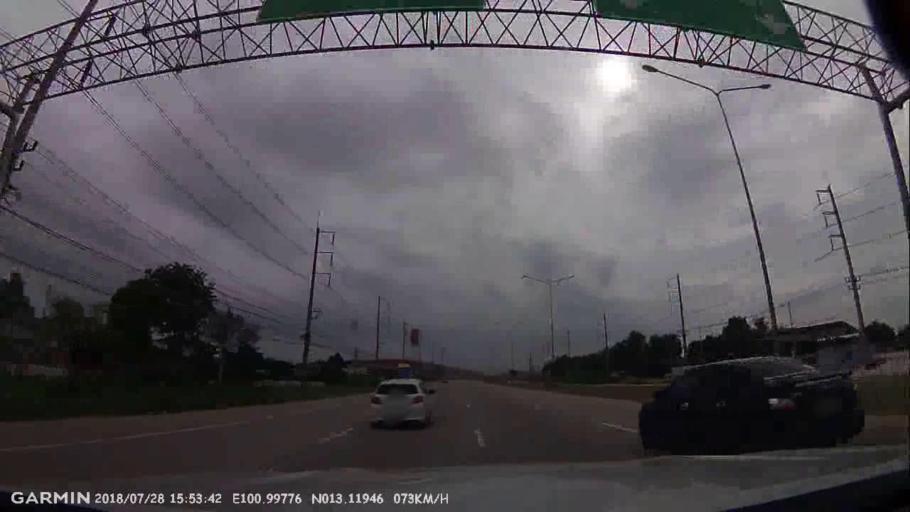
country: TH
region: Chon Buri
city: Ban Talat Bueng
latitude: 13.1194
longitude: 100.9975
